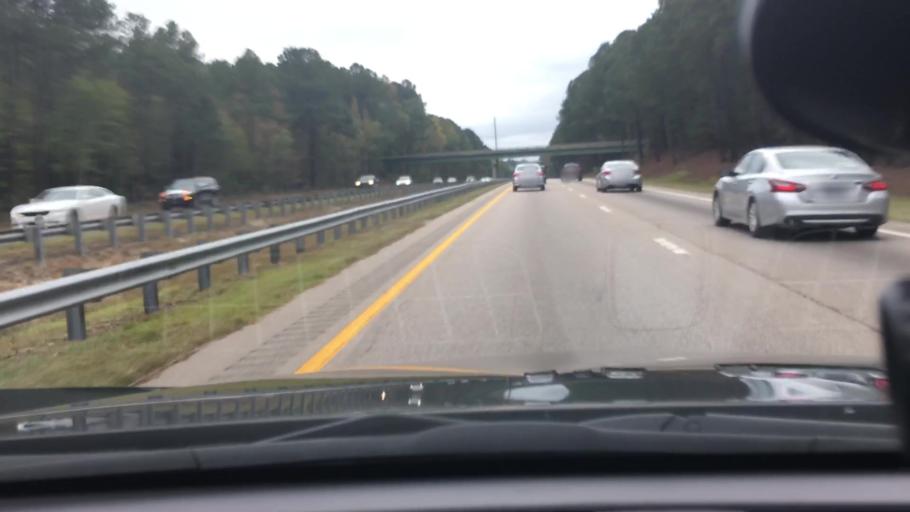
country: US
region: North Carolina
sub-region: Wake County
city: Wendell
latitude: 35.8175
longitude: -78.3979
